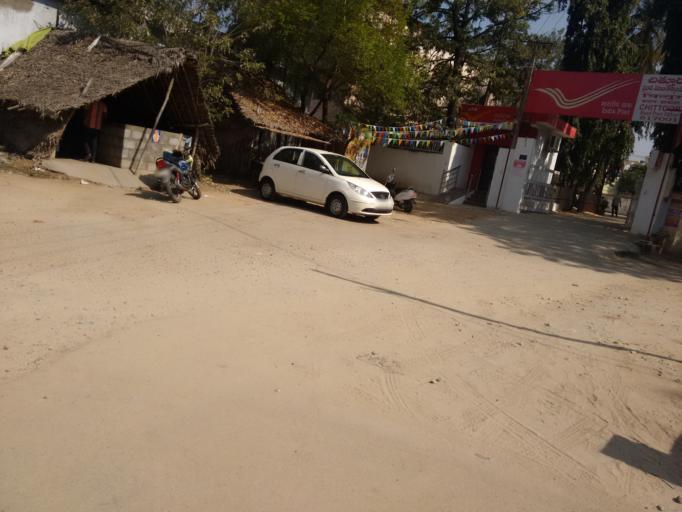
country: IN
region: Andhra Pradesh
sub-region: Chittoor
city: Chittoor
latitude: 13.2158
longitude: 79.1007
